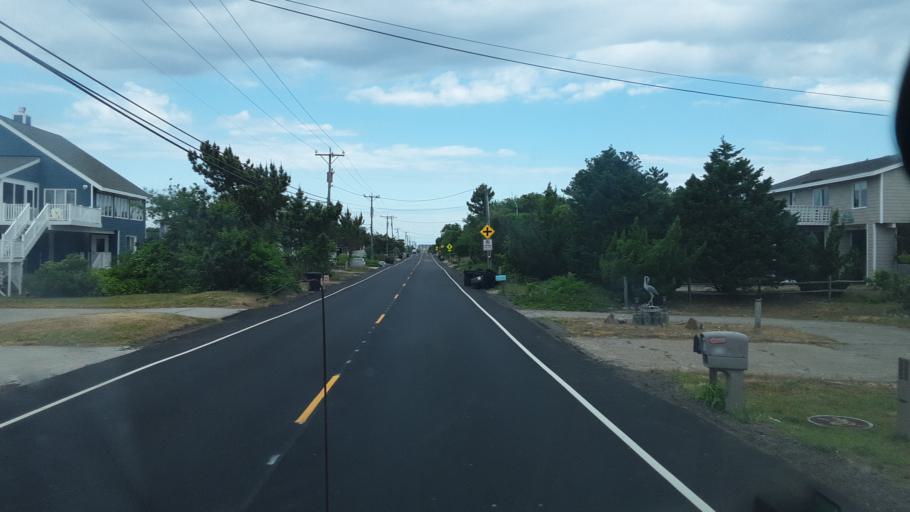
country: US
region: Virginia
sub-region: City of Virginia Beach
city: Virginia Beach
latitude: 36.7309
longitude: -75.9395
